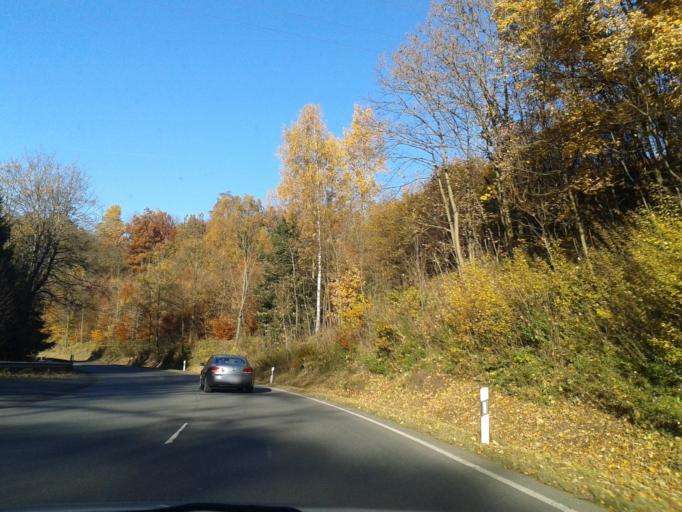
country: DE
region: North Rhine-Westphalia
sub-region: Regierungsbezirk Arnsberg
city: Winterberg
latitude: 51.2529
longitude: 8.5303
